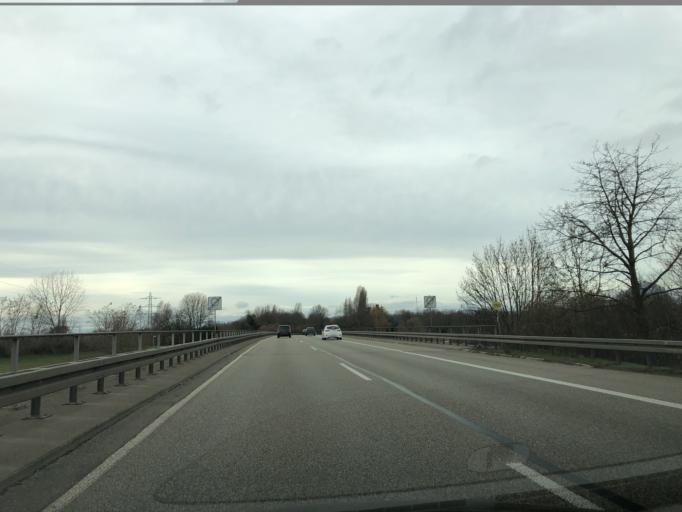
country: DE
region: Baden-Wuerttemberg
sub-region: Freiburg Region
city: Freiburg
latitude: 48.0034
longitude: 7.8087
